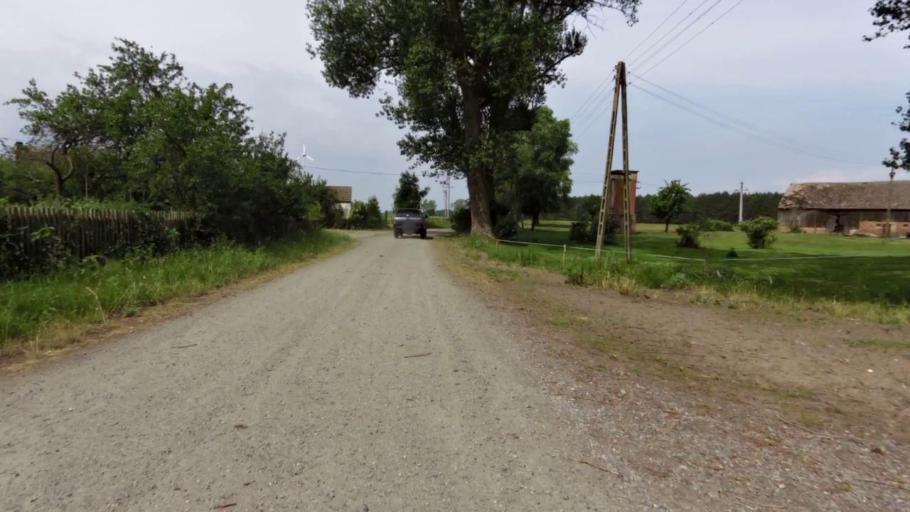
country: PL
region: West Pomeranian Voivodeship
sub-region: Powiat kamienski
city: Wolin
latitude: 53.7649
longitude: 14.6488
